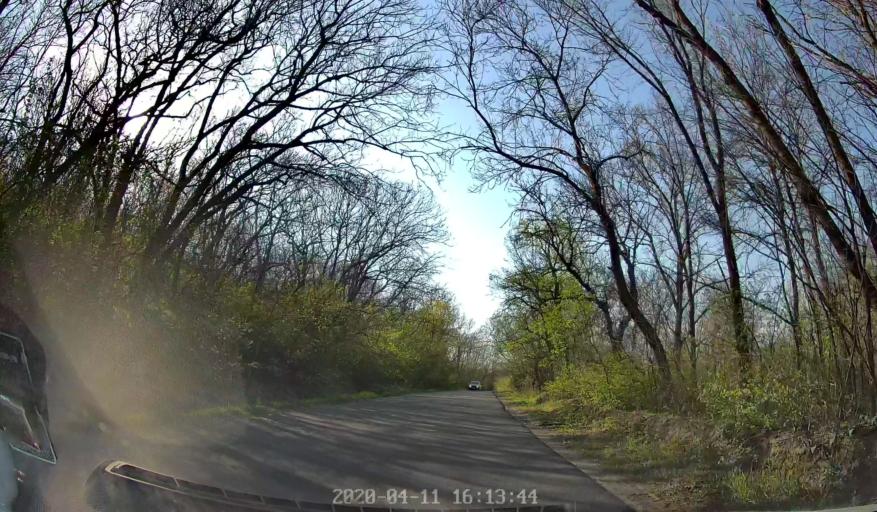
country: MD
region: Chisinau
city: Vadul lui Voda
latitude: 47.0728
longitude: 29.1082
